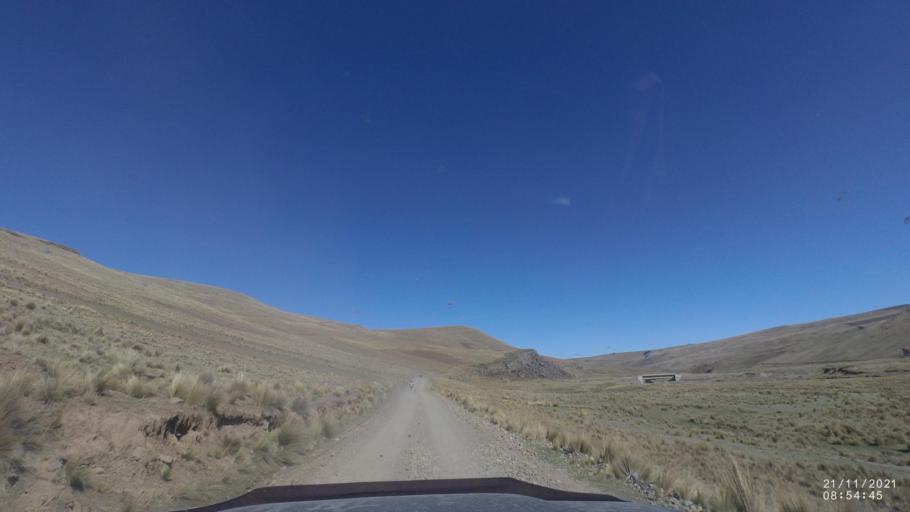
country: BO
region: Cochabamba
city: Cochabamba
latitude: -17.2017
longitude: -66.2448
